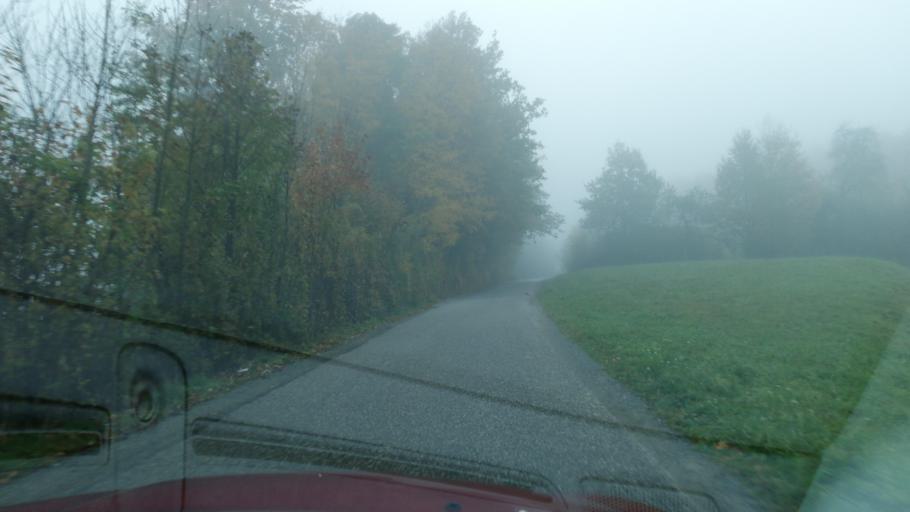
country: AT
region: Upper Austria
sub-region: Politischer Bezirk Grieskirchen
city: Bad Schallerbach
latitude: 48.2163
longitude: 13.8817
